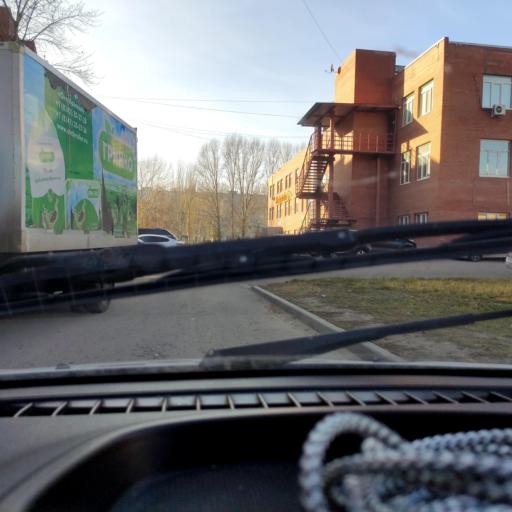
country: RU
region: Samara
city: Tol'yatti
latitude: 53.5103
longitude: 49.4533
